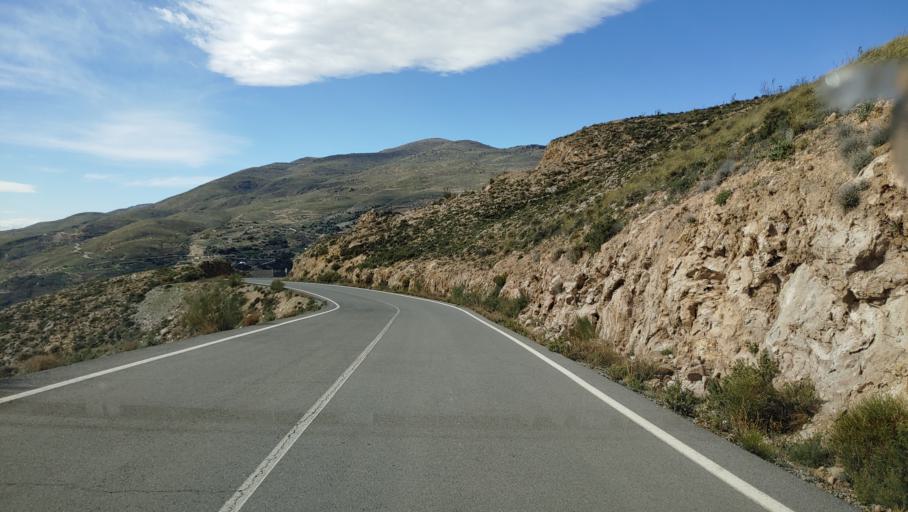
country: ES
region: Andalusia
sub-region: Provincia de Almeria
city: Ohanes
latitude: 37.0311
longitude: -2.7342
